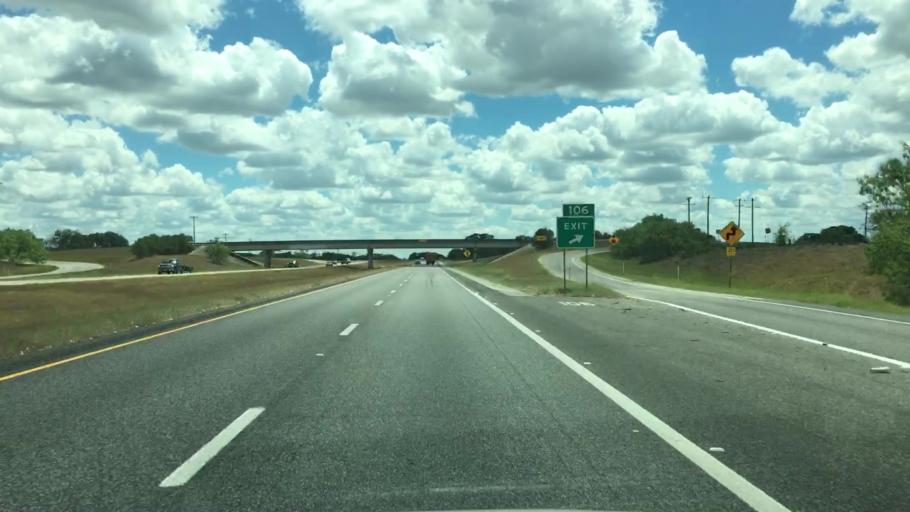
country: US
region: Texas
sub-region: Atascosa County
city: Pleasanton
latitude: 28.9476
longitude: -98.4372
